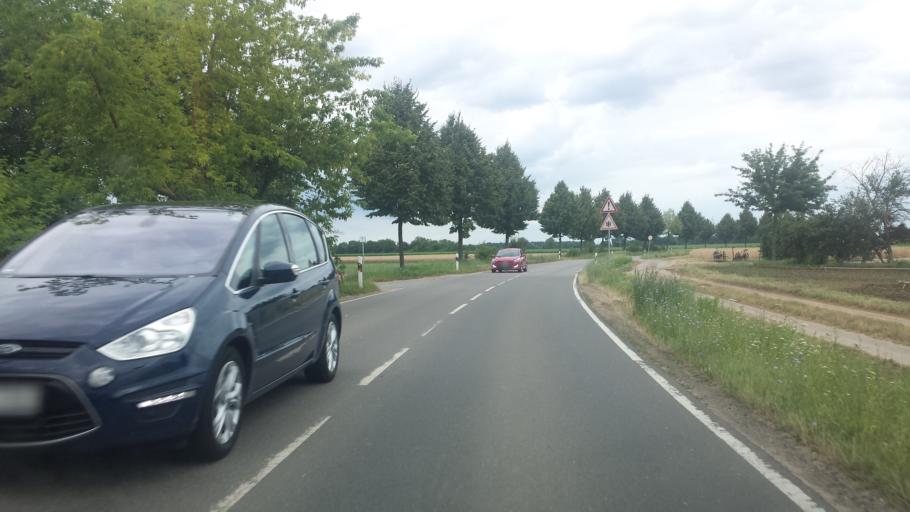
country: DE
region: Rheinland-Pfalz
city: Hassloch
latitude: 49.3717
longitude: 8.2394
